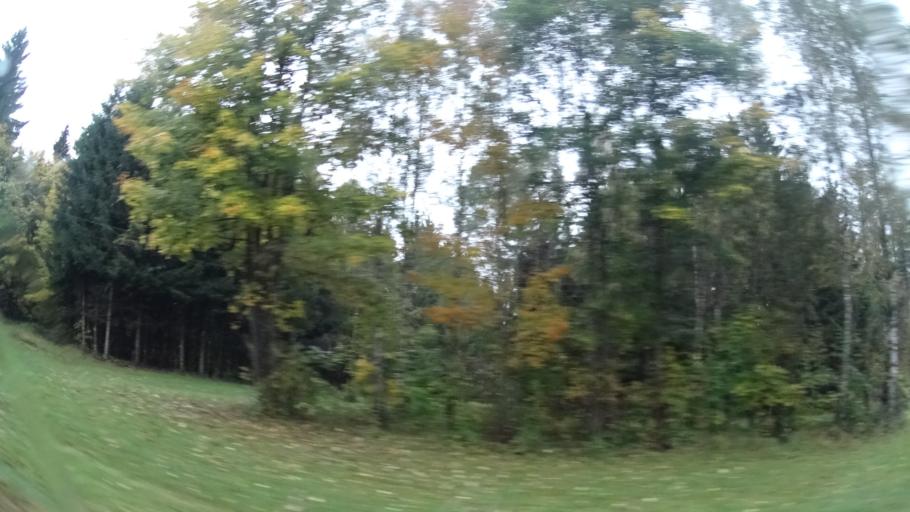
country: DE
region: Thuringia
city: Wurzbach
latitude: 50.4446
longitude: 11.5216
